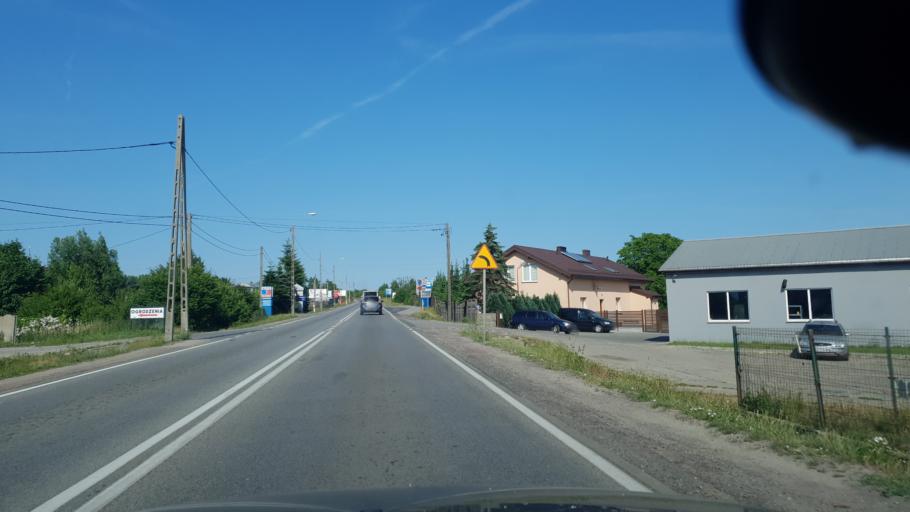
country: PL
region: Pomeranian Voivodeship
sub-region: Powiat kartuski
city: Chwaszczyno
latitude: 54.4476
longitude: 18.4286
